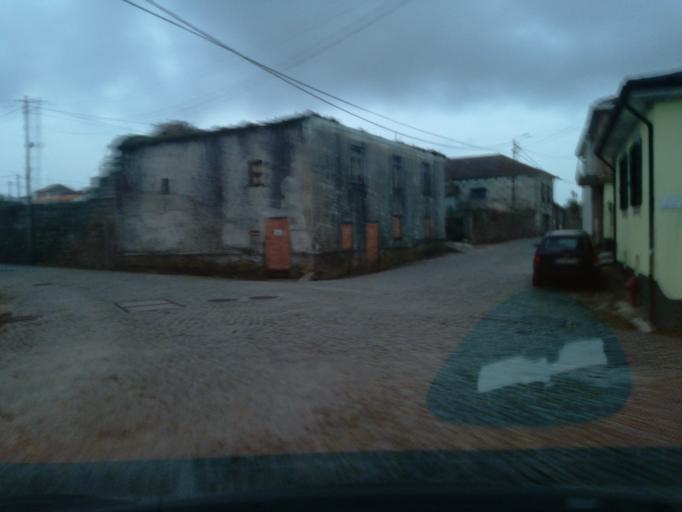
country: PT
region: Porto
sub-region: Maia
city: Gemunde
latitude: 41.2685
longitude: -8.6637
